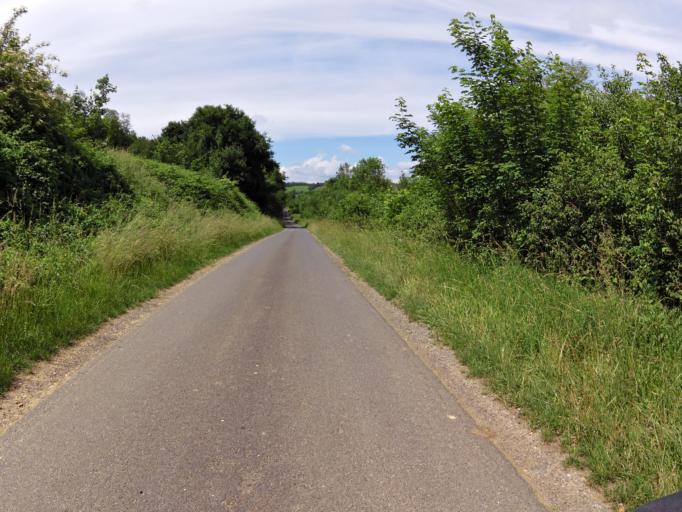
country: FR
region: Champagne-Ardenne
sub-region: Departement des Ardennes
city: Mouzon
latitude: 49.5362
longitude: 5.0879
